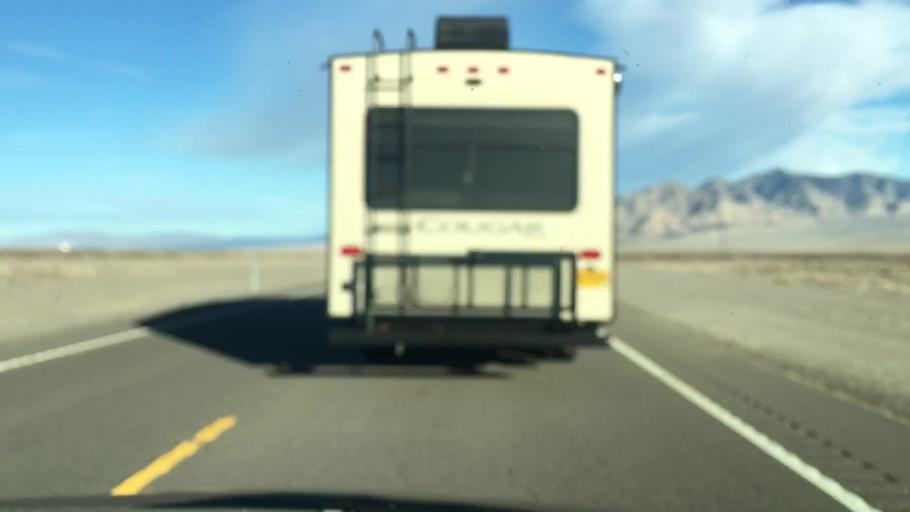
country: US
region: Nevada
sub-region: Nye County
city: Tonopah
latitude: 38.0331
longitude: -117.7000
